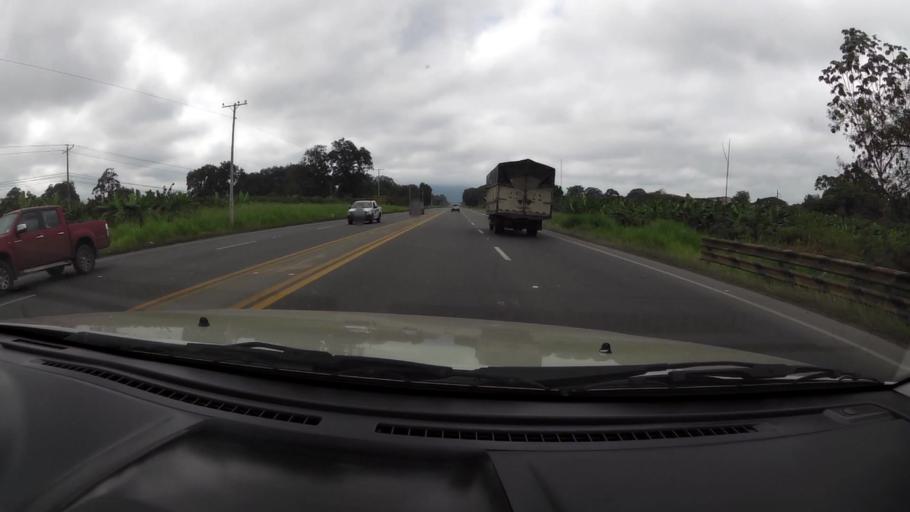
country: EC
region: Guayas
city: Naranjal
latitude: -2.6468
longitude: -79.6173
